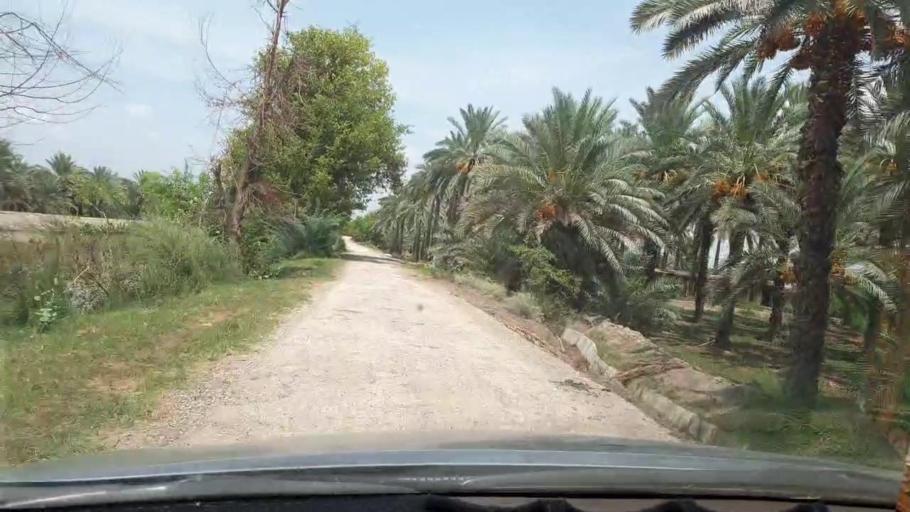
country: PK
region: Sindh
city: Khairpur
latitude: 27.4569
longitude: 68.8008
